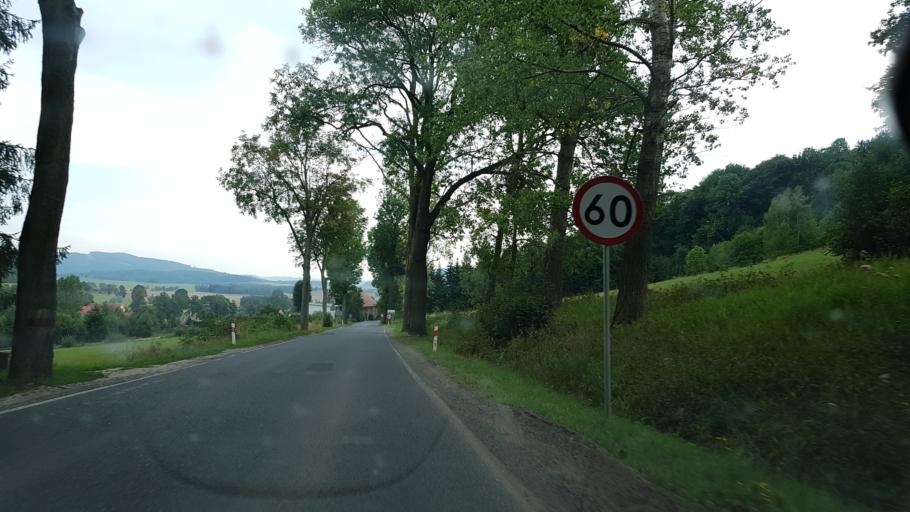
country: PL
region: Lower Silesian Voivodeship
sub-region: Powiat kamiennogorski
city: Marciszow
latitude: 50.8884
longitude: 15.9946
